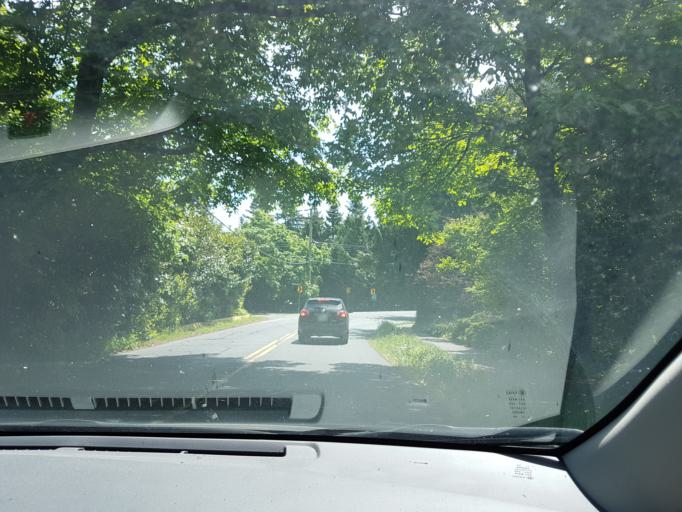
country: CA
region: British Columbia
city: Oak Bay
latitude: 48.4823
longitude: -123.3048
